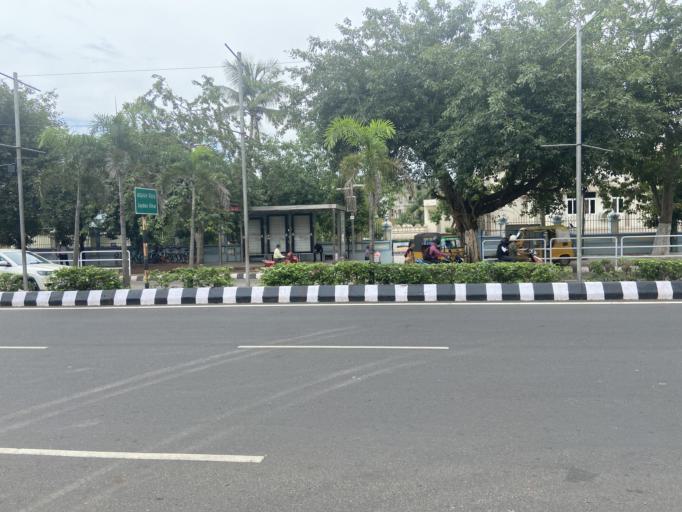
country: IN
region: Odisha
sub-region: Khordha
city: Bhubaneshwar
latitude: 20.2943
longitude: 85.8251
